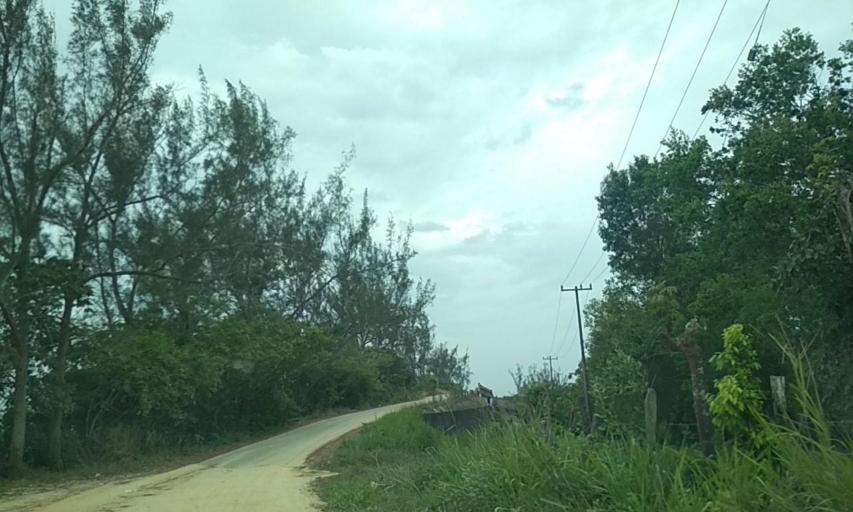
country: MX
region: Veracruz
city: Las Choapas
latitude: 17.8858
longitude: -94.1243
